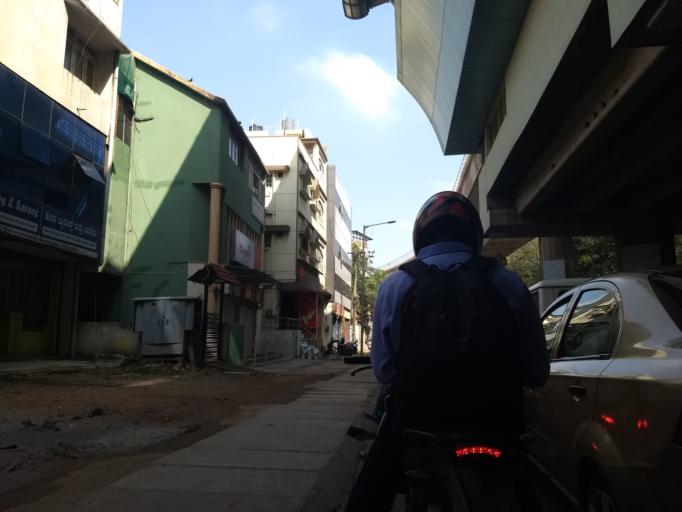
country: IN
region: Karnataka
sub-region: Bangalore Urban
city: Bangalore
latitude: 12.9468
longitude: 77.5799
